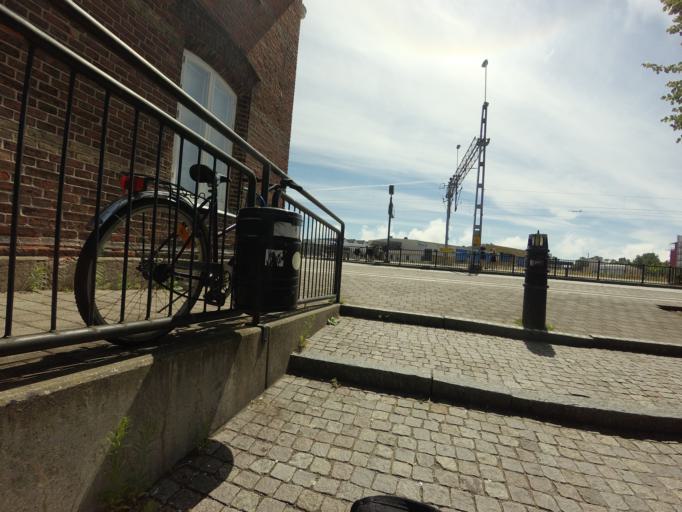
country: SE
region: Skane
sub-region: Simrishamns Kommun
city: Simrishamn
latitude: 55.5543
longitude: 14.3527
